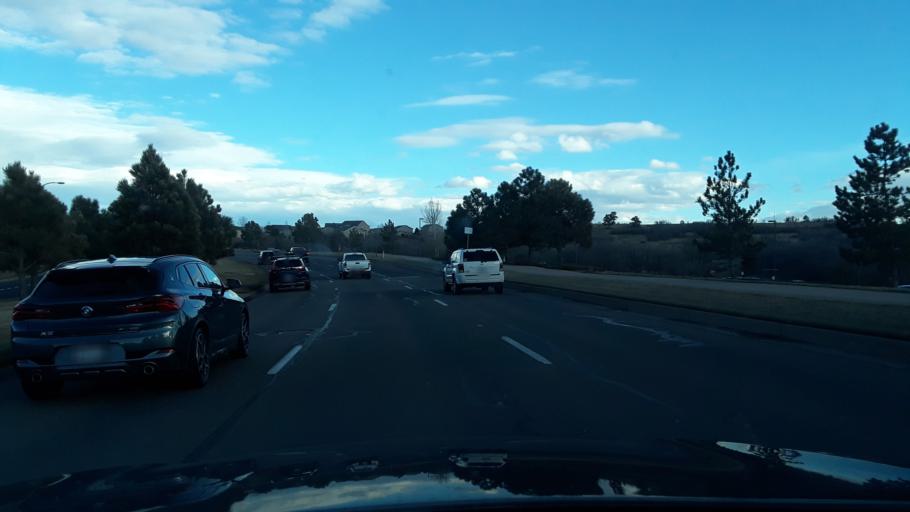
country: US
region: Colorado
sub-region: El Paso County
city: Gleneagle
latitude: 39.0091
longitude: -104.8066
